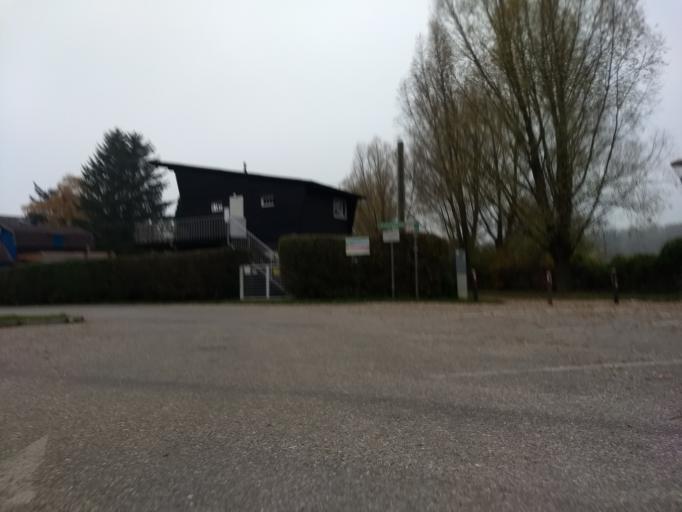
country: AT
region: Lower Austria
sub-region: Politischer Bezirk Tulln
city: Wordern
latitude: 48.3451
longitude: 16.2394
